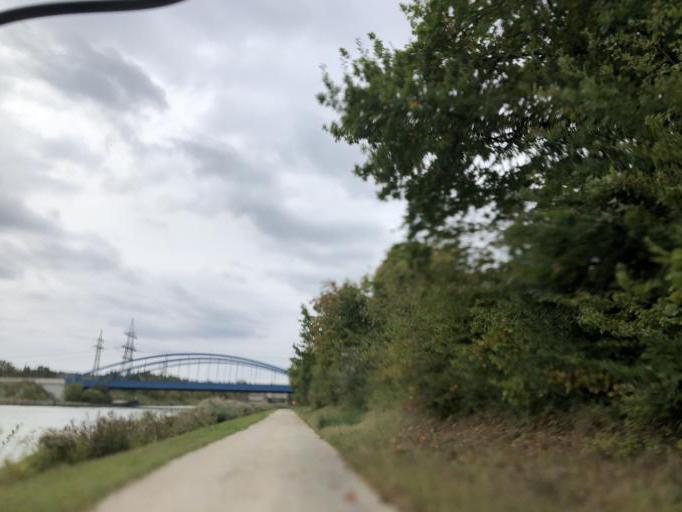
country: DE
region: Bavaria
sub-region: Regierungsbezirk Mittelfranken
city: Erlangen
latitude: 49.5624
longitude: 10.9699
